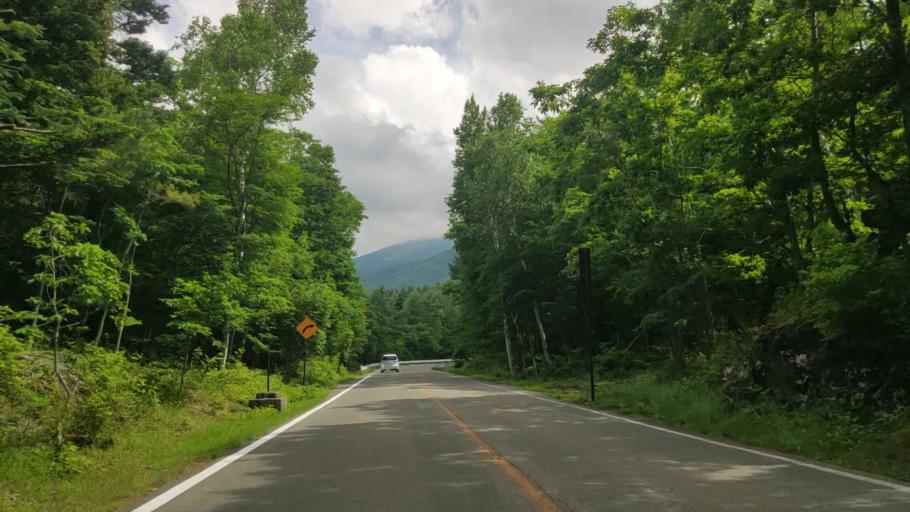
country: JP
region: Yamanashi
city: Fujikawaguchiko
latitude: 35.4280
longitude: 138.7394
